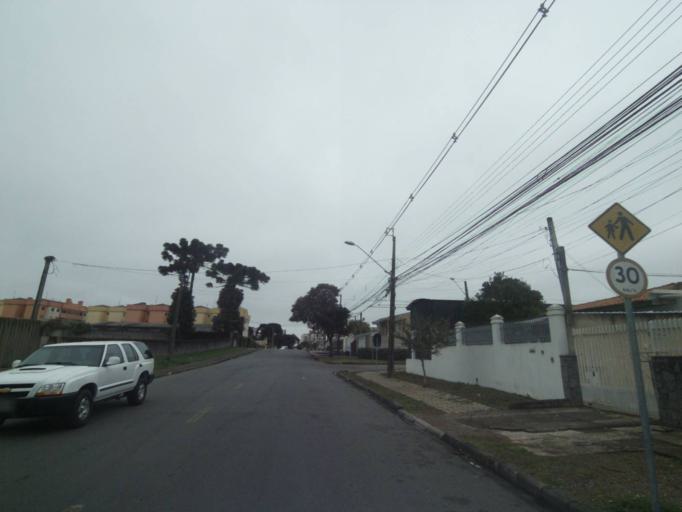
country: BR
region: Parana
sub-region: Curitiba
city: Curitiba
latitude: -25.5016
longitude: -49.3041
